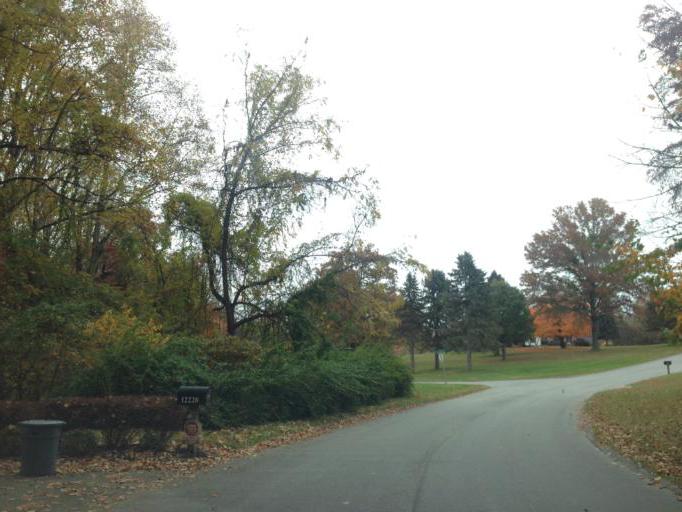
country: US
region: Maryland
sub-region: Howard County
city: Highland
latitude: 39.2759
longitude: -76.9343
